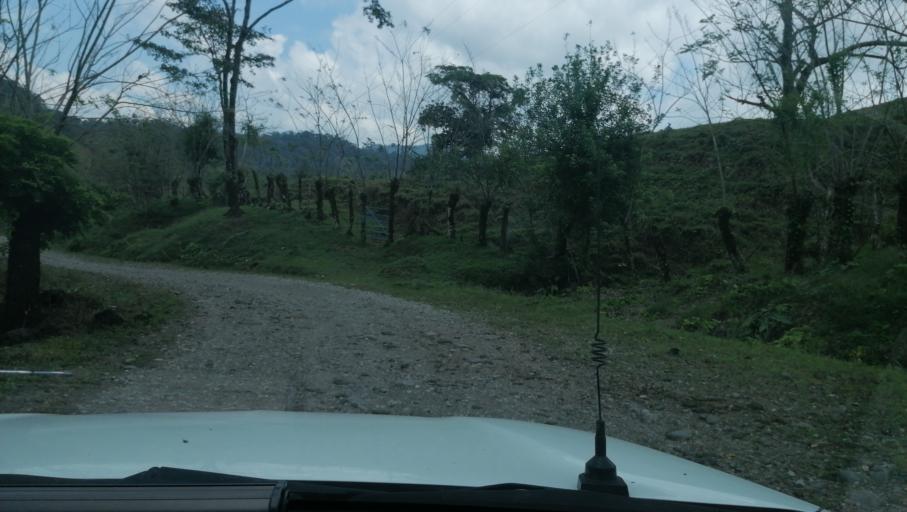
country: MX
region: Chiapas
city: Ixtacomitan
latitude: 17.4400
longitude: -93.2007
